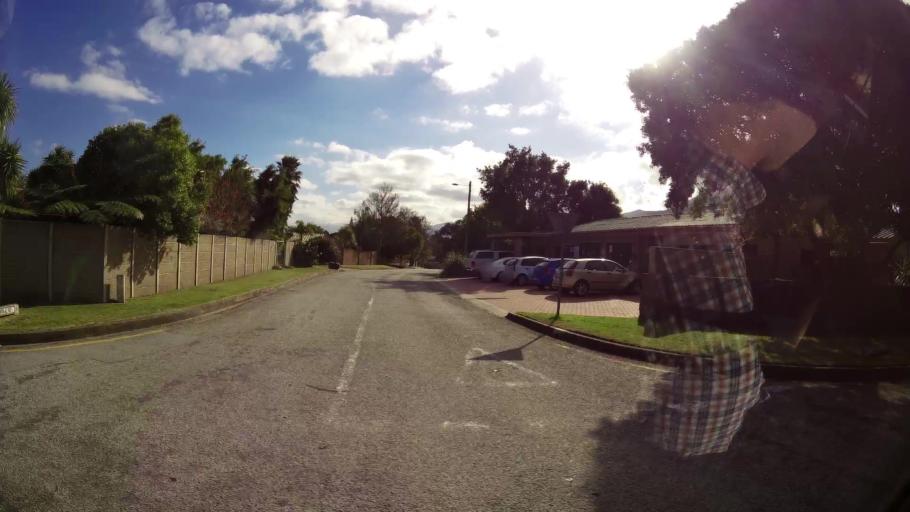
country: ZA
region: Western Cape
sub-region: Eden District Municipality
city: George
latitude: -33.9581
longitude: 22.4838
